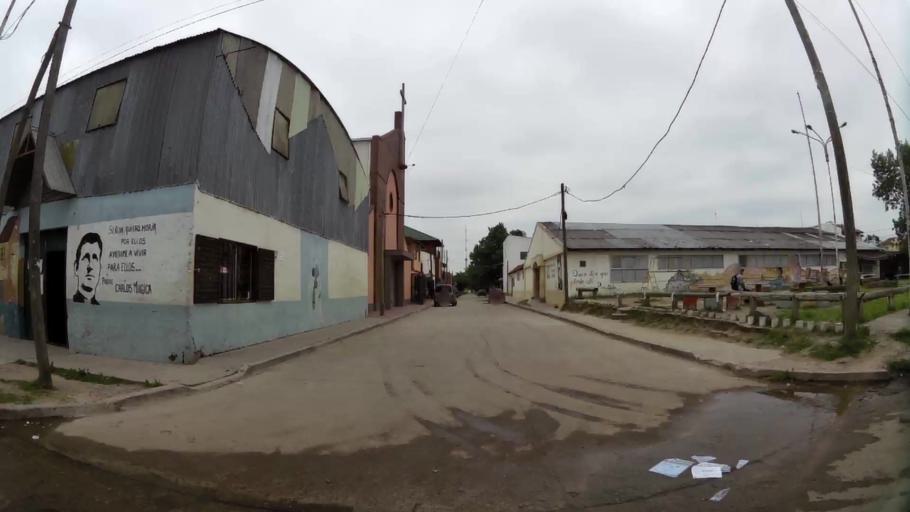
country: AR
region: Buenos Aires
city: San Justo
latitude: -34.6961
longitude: -58.5480
